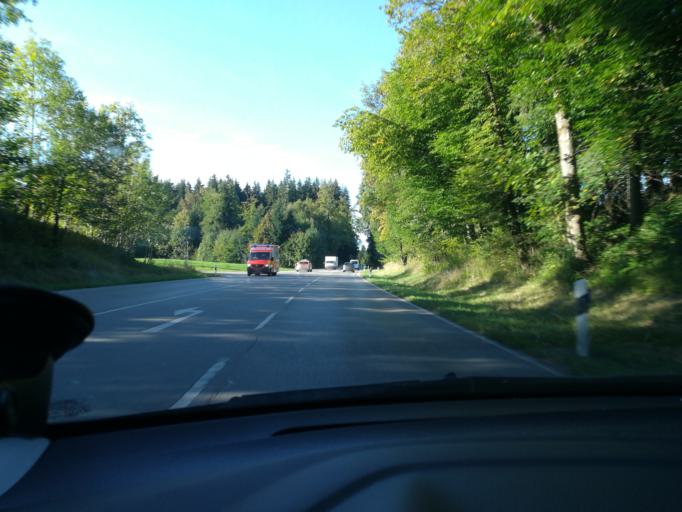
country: DE
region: Bavaria
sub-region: Upper Bavaria
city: Miesbach
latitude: 47.8140
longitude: 11.8381
